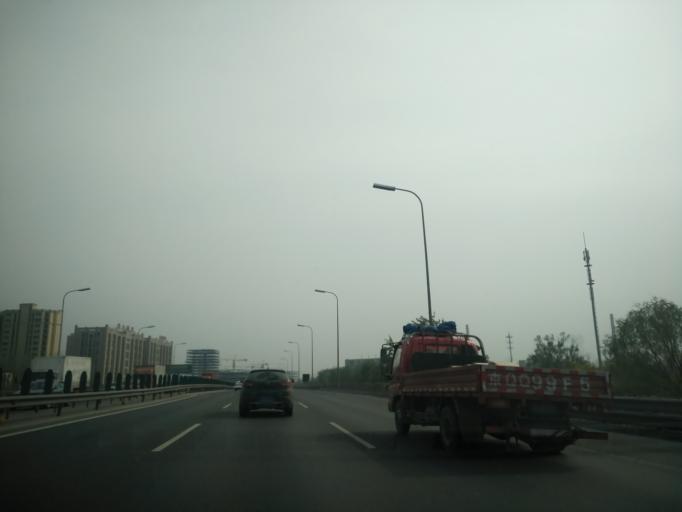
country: CN
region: Beijing
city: Dongfeng
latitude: 39.8576
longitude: 116.5429
